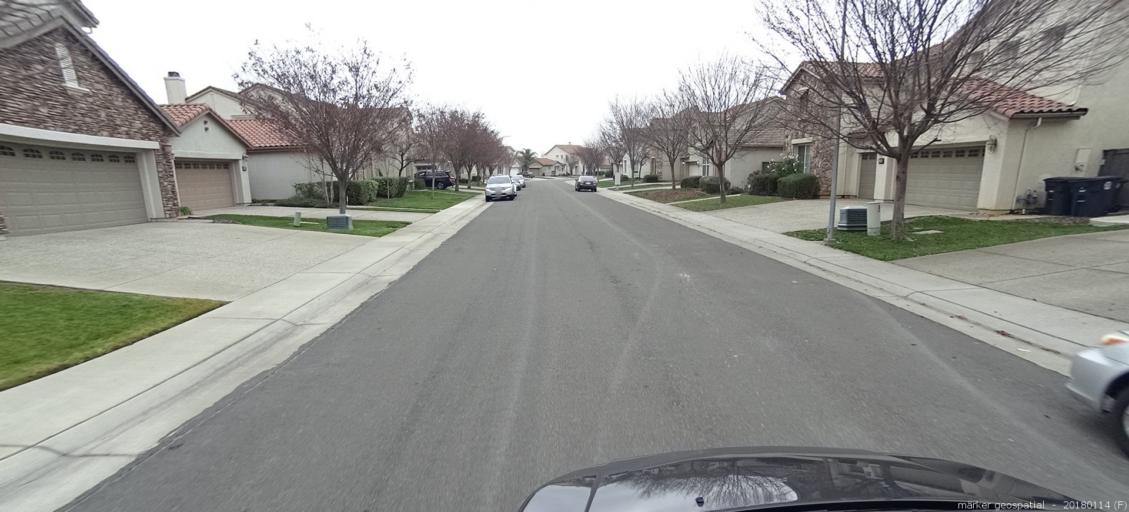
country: US
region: California
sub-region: Sacramento County
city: Gold River
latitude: 38.5514
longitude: -121.2343
